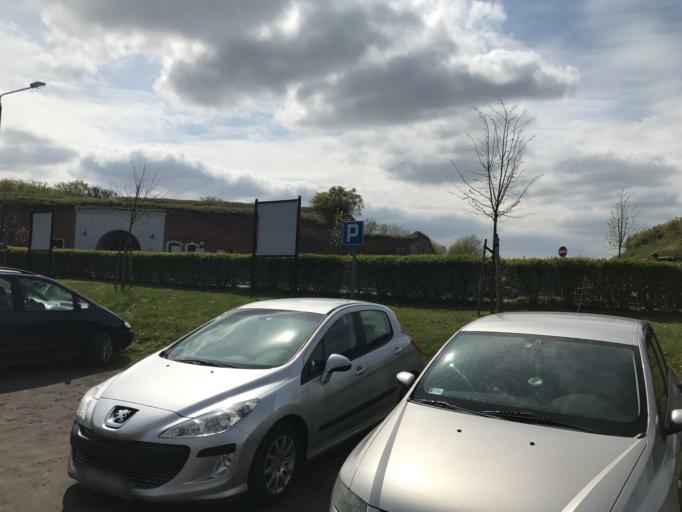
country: PL
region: Kujawsko-Pomorskie
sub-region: Grudziadz
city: Grudziadz
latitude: 53.5106
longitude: 18.7619
